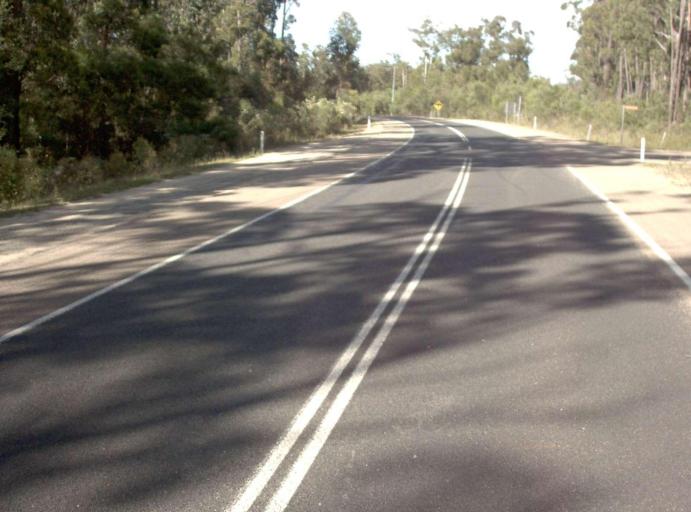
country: AU
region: Victoria
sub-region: East Gippsland
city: Lakes Entrance
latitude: -37.6896
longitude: 148.0437
